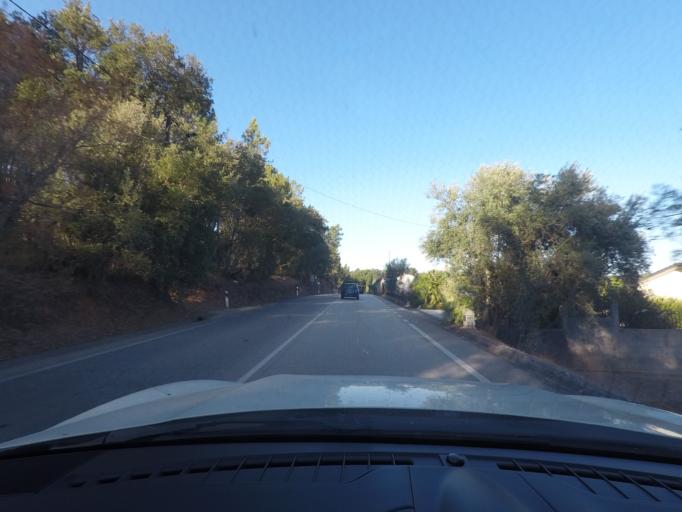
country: PT
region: Coimbra
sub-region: Vila Nova de Poiares
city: Poiares
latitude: 40.1863
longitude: -8.2574
